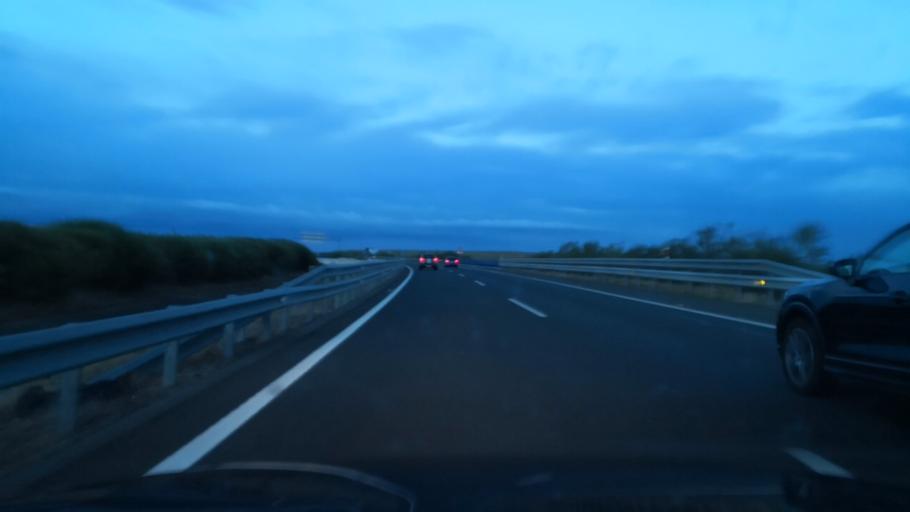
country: ES
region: Extremadura
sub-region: Provincia de Caceres
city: Casar de Caceres
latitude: 39.5362
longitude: -6.4084
